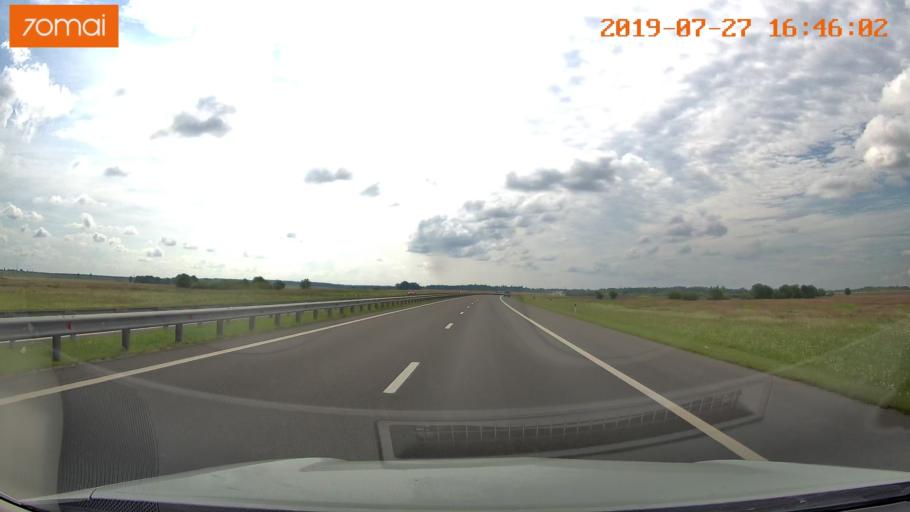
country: RU
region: Kaliningrad
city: Gvardeysk
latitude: 54.6674
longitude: 21.0329
